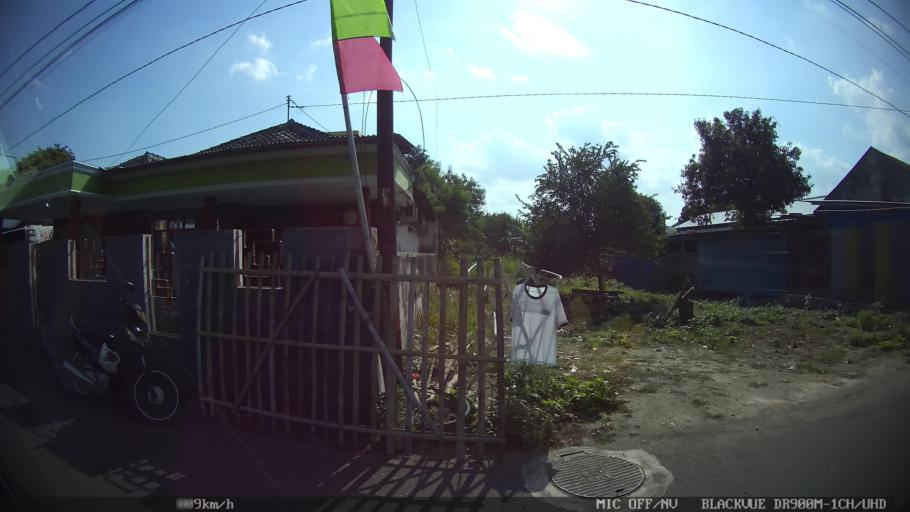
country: ID
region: Daerah Istimewa Yogyakarta
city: Sewon
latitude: -7.8336
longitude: 110.3931
